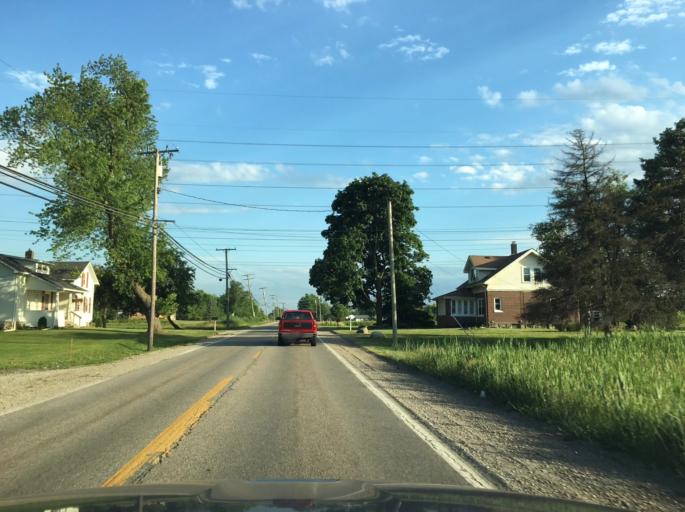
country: US
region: Michigan
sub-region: Macomb County
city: Shelby
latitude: 42.7246
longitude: -82.9598
